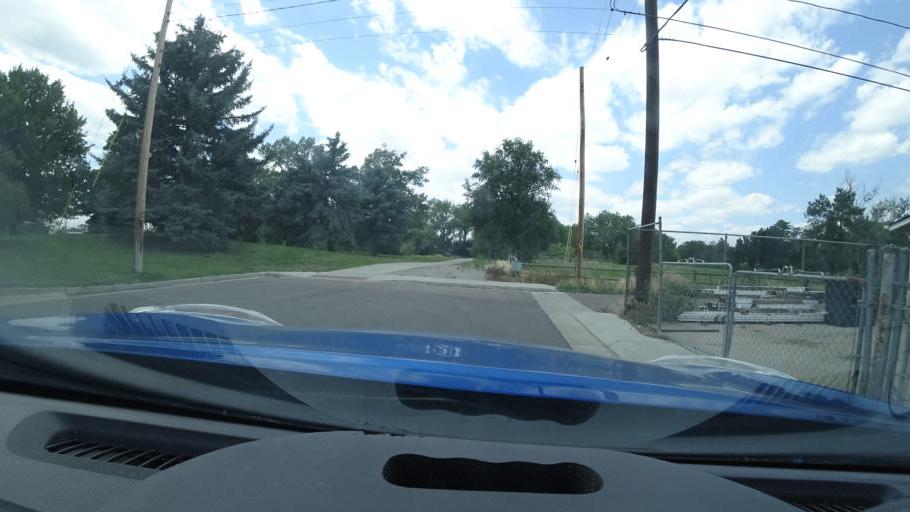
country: US
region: Colorado
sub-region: Arapahoe County
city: Englewood
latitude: 39.6804
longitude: -104.9975
